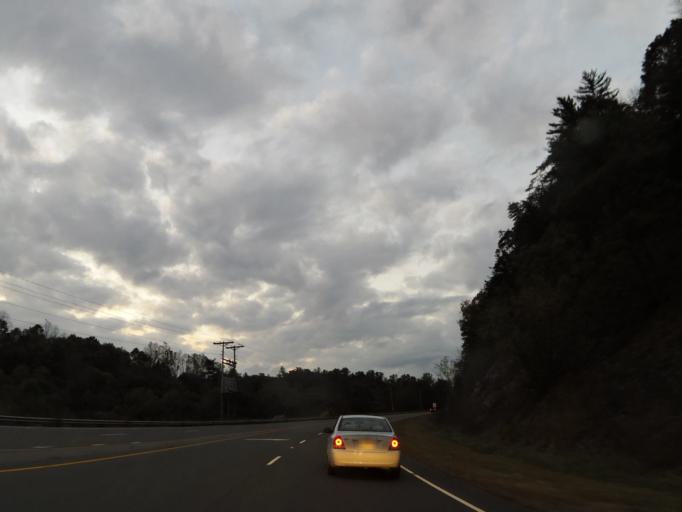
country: US
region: North Carolina
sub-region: Madison County
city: Marshall
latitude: 35.7878
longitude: -82.6537
